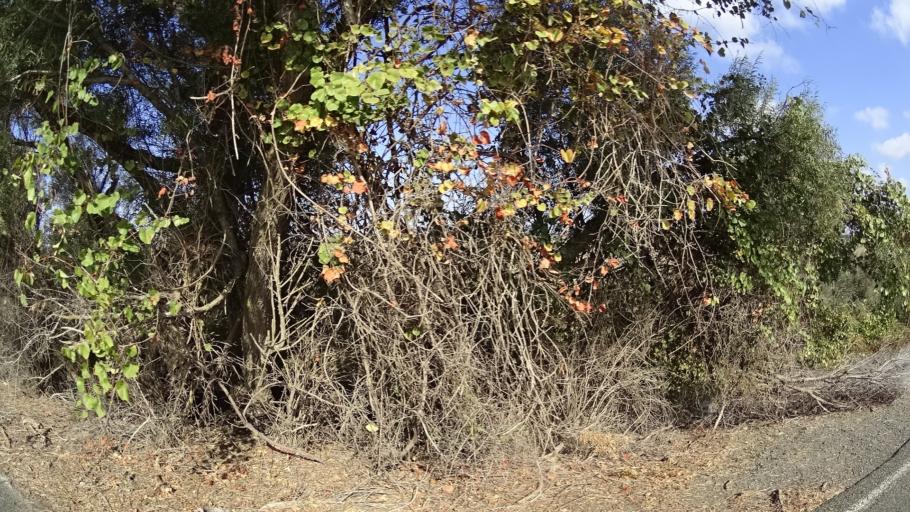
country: US
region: California
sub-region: Yolo County
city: Woodland
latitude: 38.7487
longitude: -121.7129
